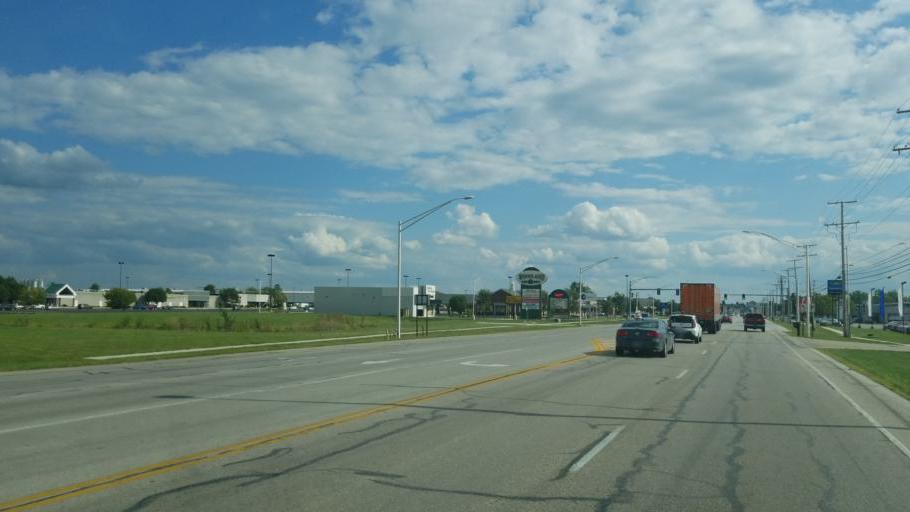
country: US
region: Ohio
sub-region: Wood County
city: Bowling Green
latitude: 41.3997
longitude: -83.6507
